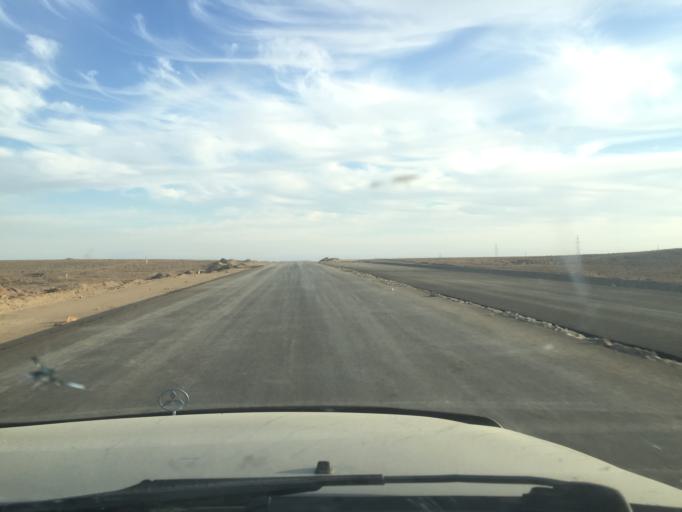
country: KZ
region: Zhambyl
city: Mynaral
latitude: 45.2671
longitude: 73.7936
